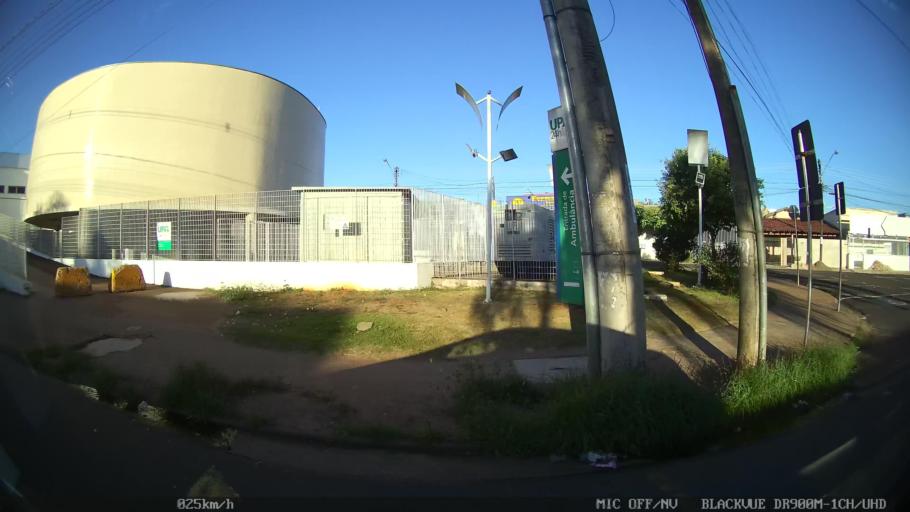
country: BR
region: Sao Paulo
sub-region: Sao Jose Do Rio Preto
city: Sao Jose do Rio Preto
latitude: -20.7779
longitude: -49.3667
